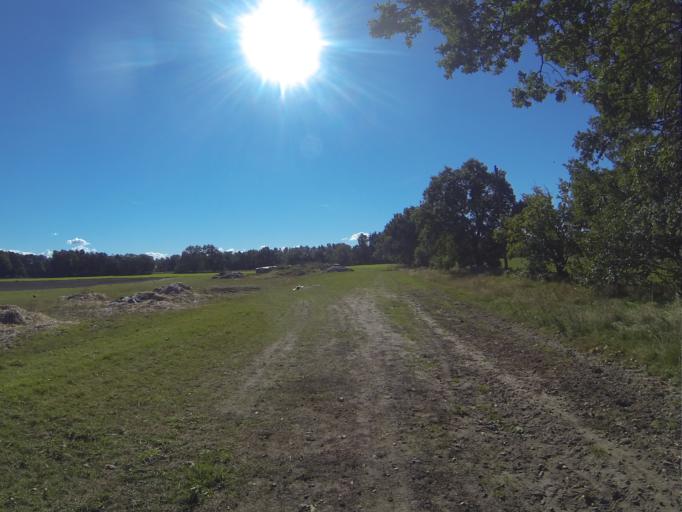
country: SE
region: Skane
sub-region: Hoors Kommun
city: Loberod
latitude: 55.7273
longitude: 13.4097
